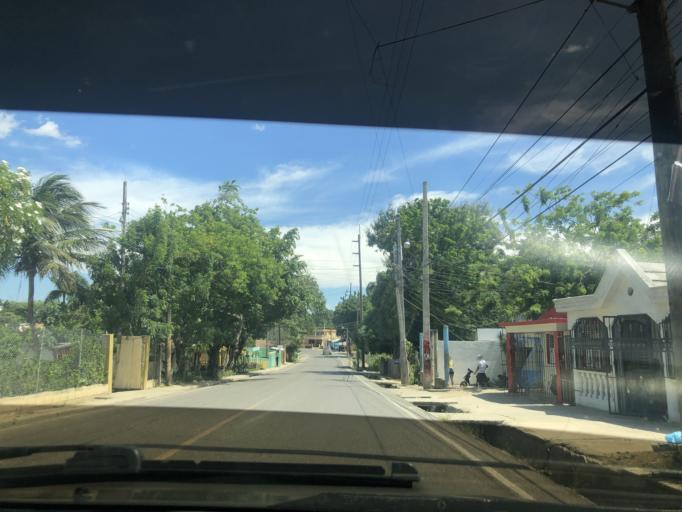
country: DO
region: Santiago
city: Santiago de los Caballeros
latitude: 19.4046
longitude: -70.6707
